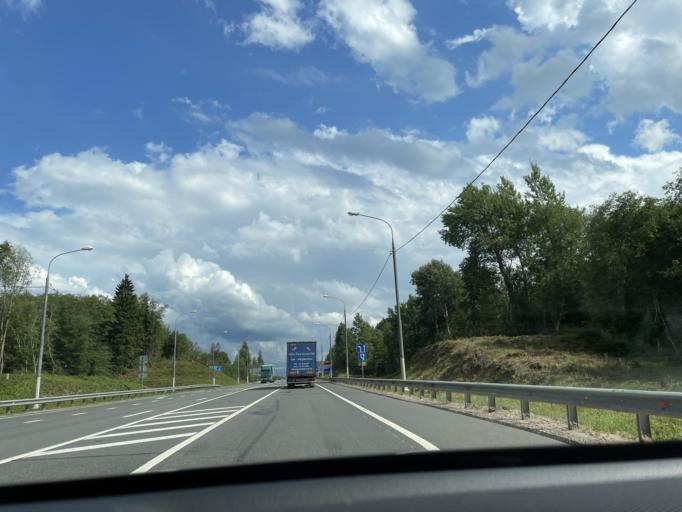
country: RU
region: Novgorod
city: Valday
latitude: 57.9507
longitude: 33.3035
